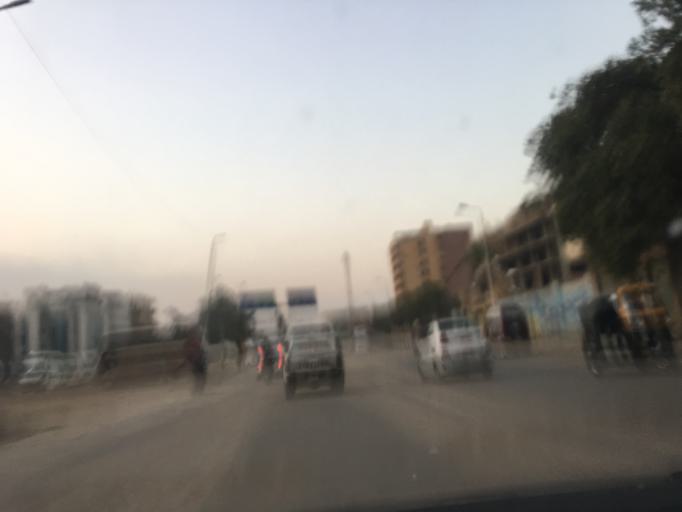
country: EG
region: Al Jizah
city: Al Jizah
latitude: 29.9919
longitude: 31.1304
